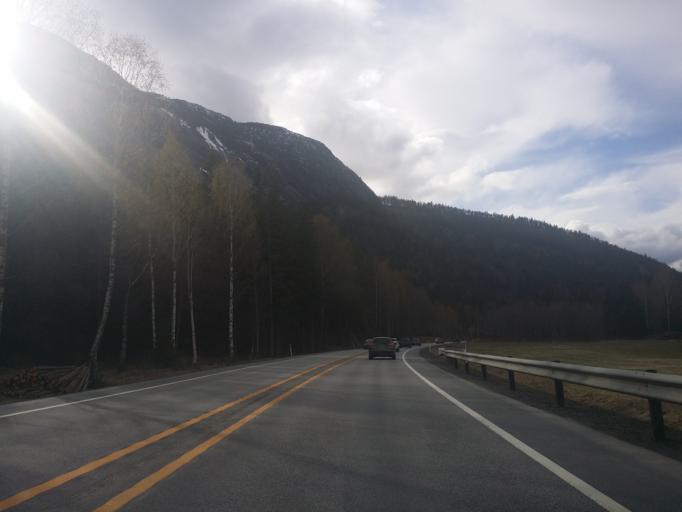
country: NO
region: Buskerud
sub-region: Fla
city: Fla
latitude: 60.4449
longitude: 9.2862
